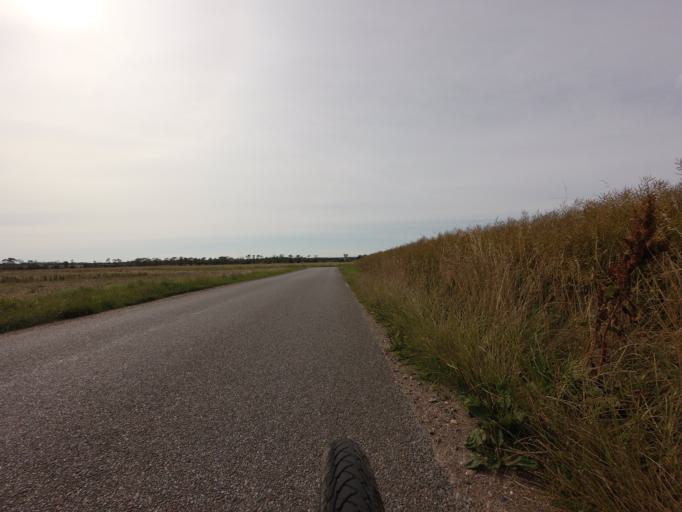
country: DK
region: North Denmark
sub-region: Hjorring Kommune
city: Hjorring
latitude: 57.4408
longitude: 9.9441
